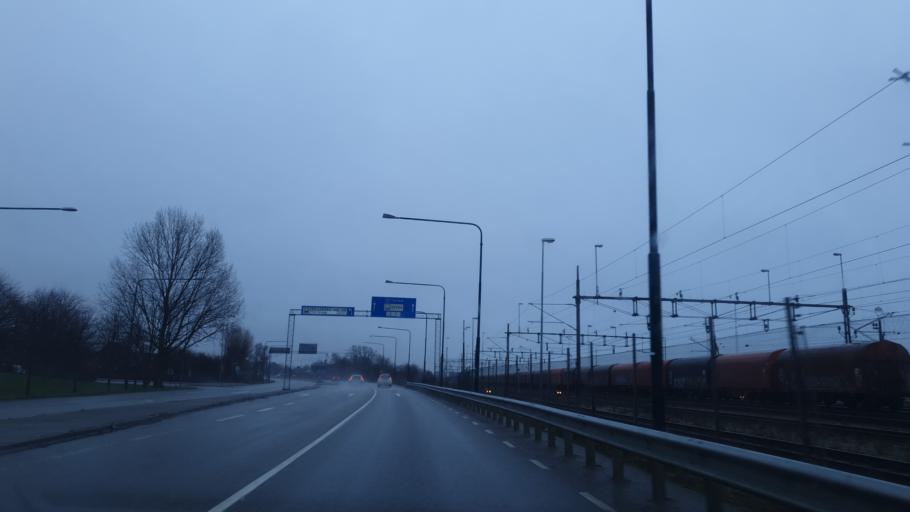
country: SE
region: Skane
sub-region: Trelleborgs Kommun
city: Trelleborg
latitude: 55.3698
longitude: 13.1708
